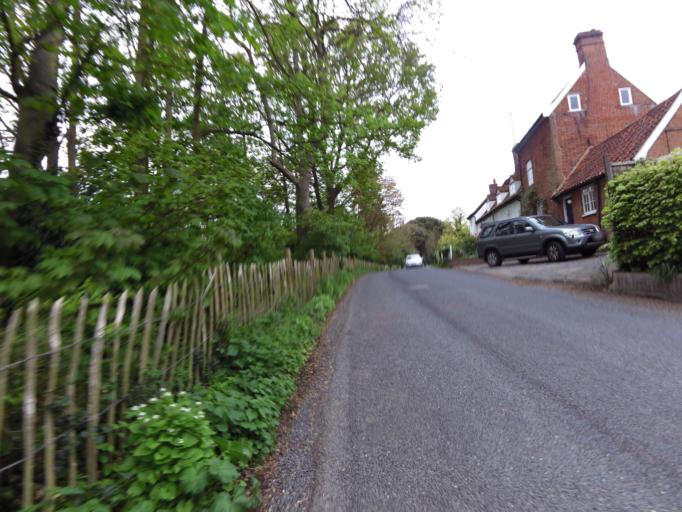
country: GB
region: England
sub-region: Suffolk
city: Kesgrave
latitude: 52.0123
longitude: 1.2329
